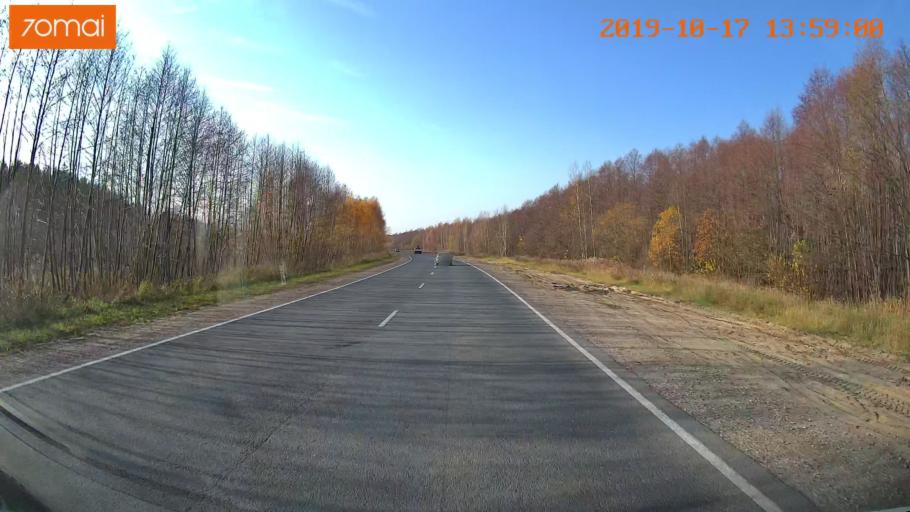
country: RU
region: Rjazan
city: Spas-Klepiki
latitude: 55.1410
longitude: 40.2130
